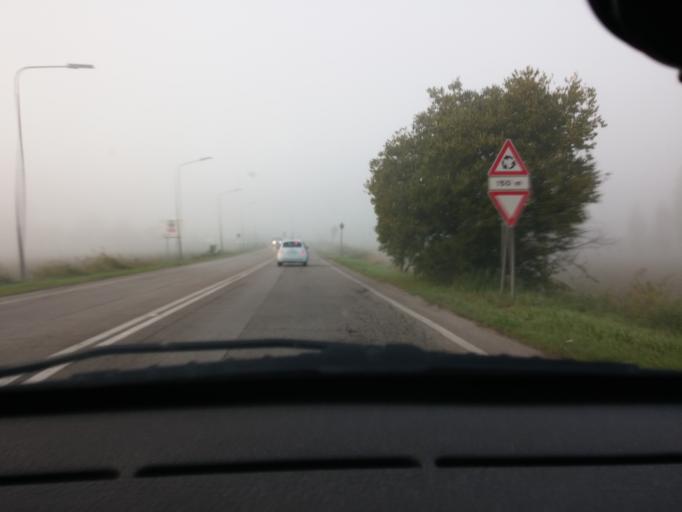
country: IT
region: Emilia-Romagna
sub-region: Provincia di Ferrara
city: Ferrara
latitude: 44.8290
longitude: 11.5938
